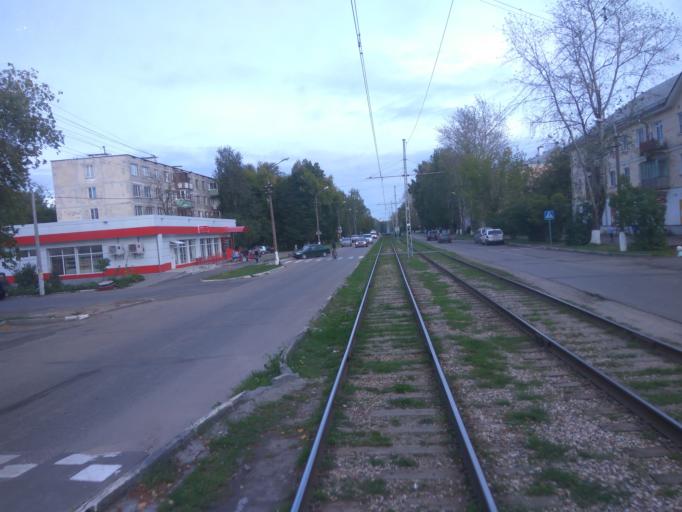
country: RU
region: Moskovskaya
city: Kolomna
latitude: 55.0770
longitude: 38.7757
